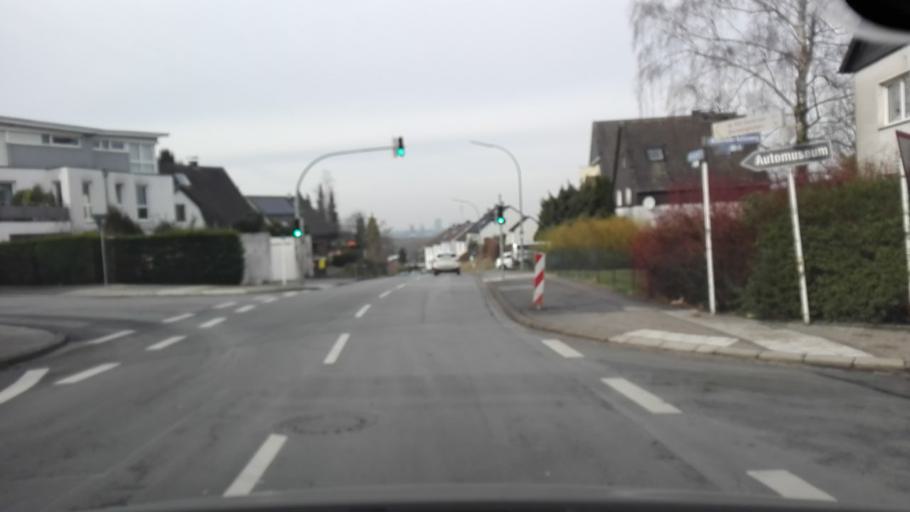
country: DE
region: North Rhine-Westphalia
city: Schwerte
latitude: 51.4660
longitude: 7.5203
